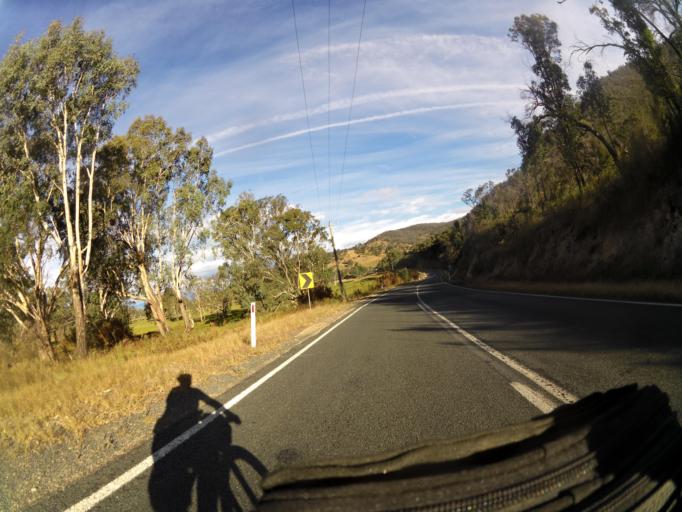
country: AU
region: New South Wales
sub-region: Greater Hume Shire
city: Holbrook
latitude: -35.9950
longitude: 147.8654
